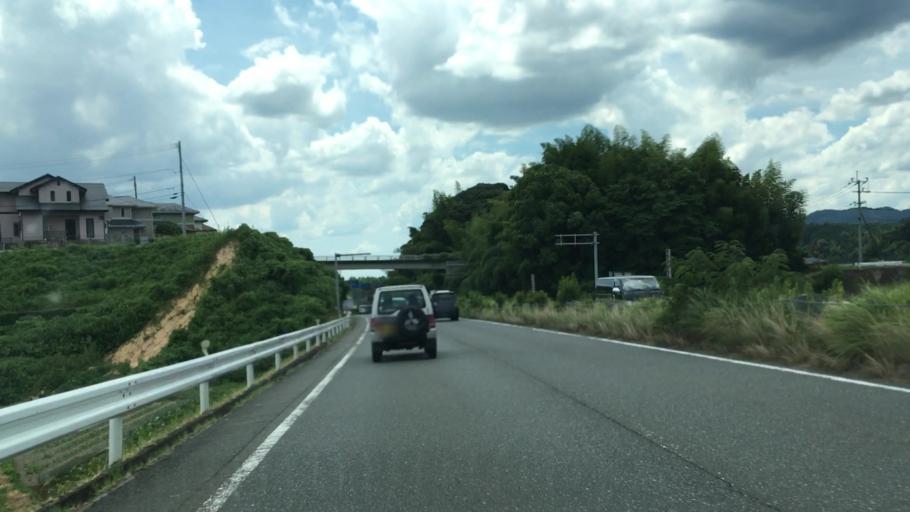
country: JP
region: Fukuoka
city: Chikushino-shi
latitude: 33.4390
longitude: 130.5260
